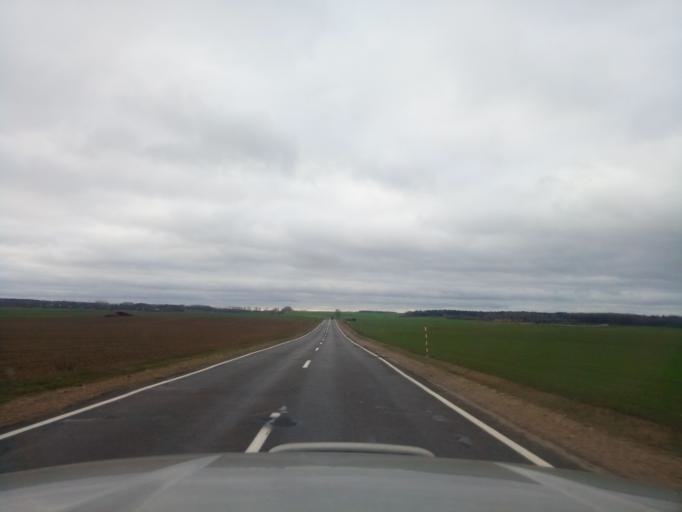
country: BY
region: Minsk
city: Kapyl'
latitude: 53.1948
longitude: 27.1961
